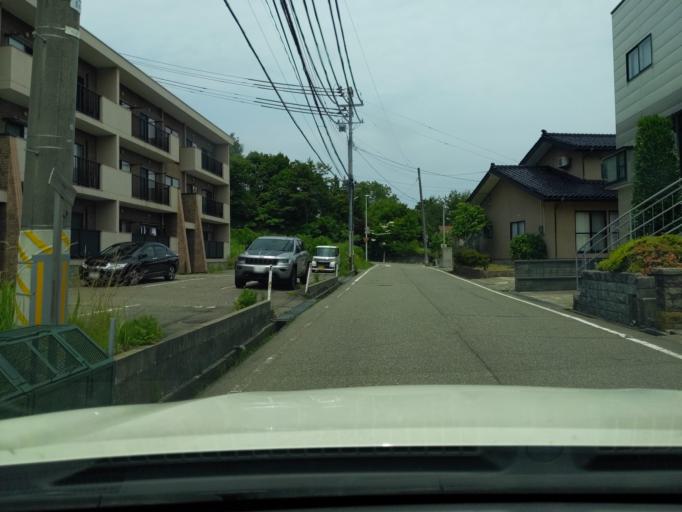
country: JP
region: Niigata
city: Kashiwazaki
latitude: 37.3558
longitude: 138.5407
